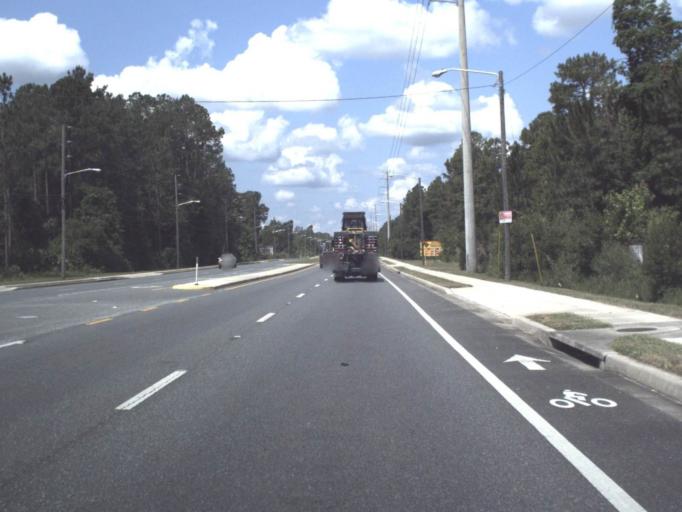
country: US
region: Florida
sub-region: Putnam County
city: Palatka
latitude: 29.6388
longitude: -81.6967
